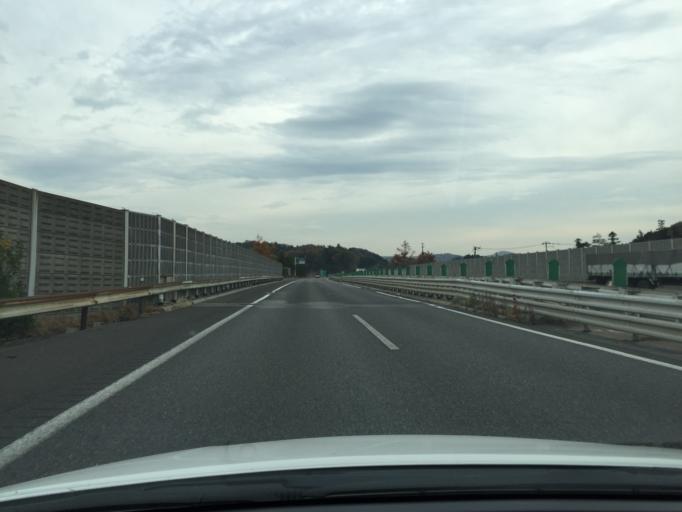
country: JP
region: Fukushima
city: Fukushima-shi
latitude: 37.7305
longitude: 140.4247
